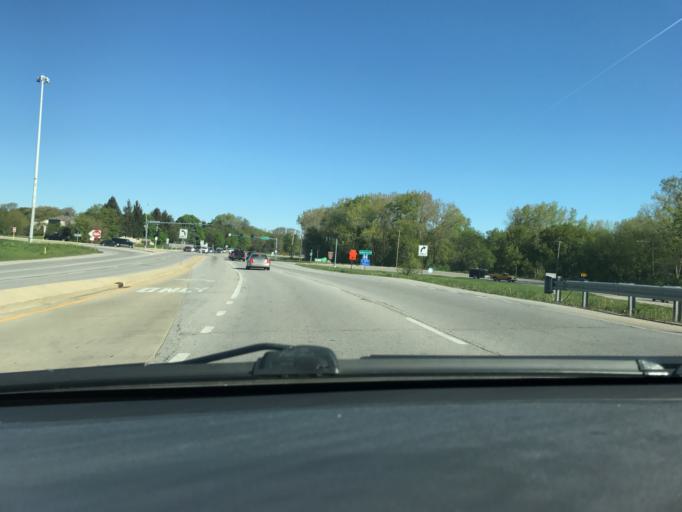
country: US
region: Illinois
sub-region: Kane County
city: Elgin
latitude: 42.0339
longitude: -88.3386
